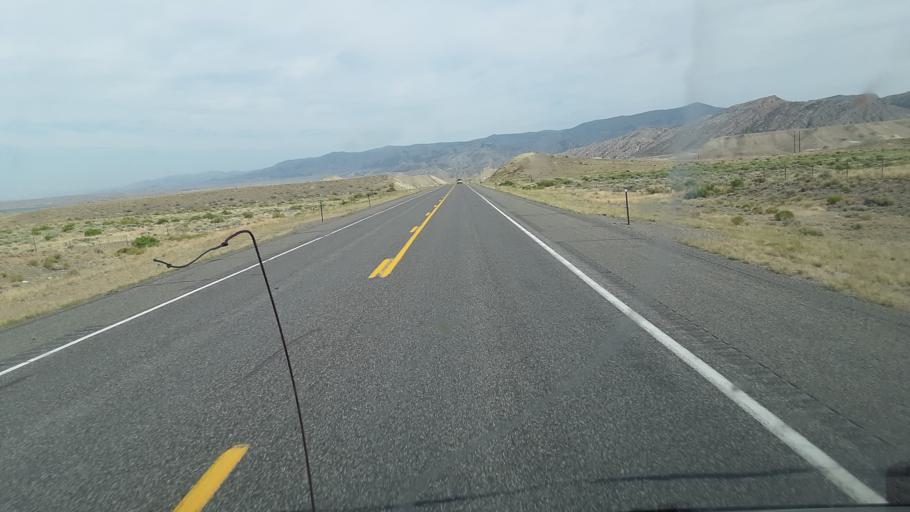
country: US
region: Wyoming
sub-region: Hot Springs County
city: Thermopolis
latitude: 43.3692
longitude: -108.1203
